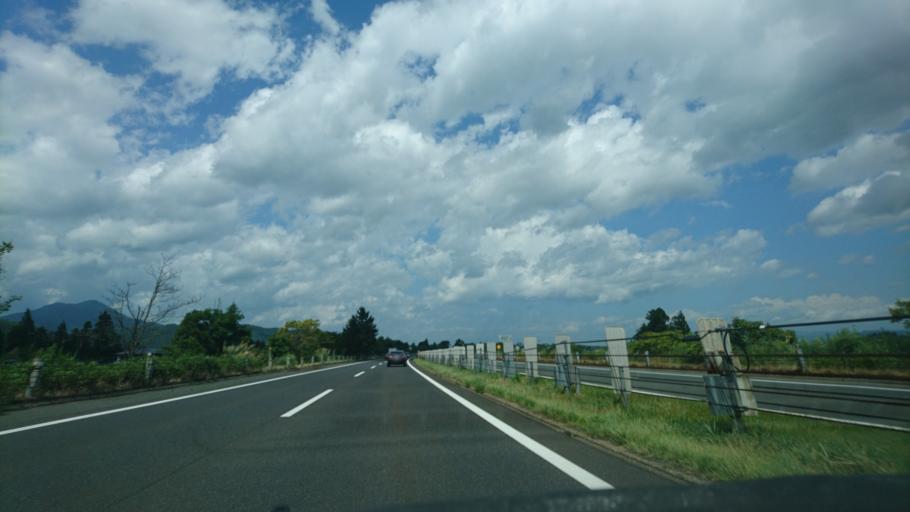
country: JP
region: Iwate
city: Morioka-shi
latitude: 39.5843
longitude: 141.1185
